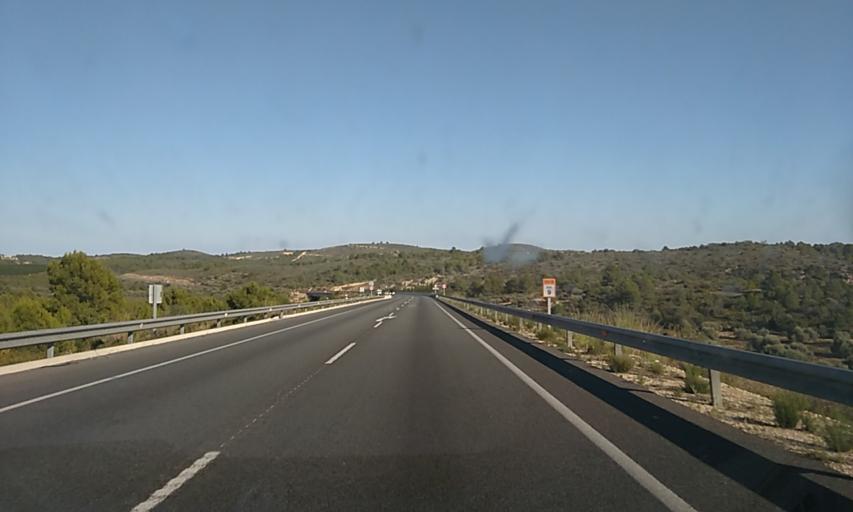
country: ES
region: Valencia
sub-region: Provincia de Castello
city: Torreblanca
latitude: 40.2104
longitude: 0.1337
